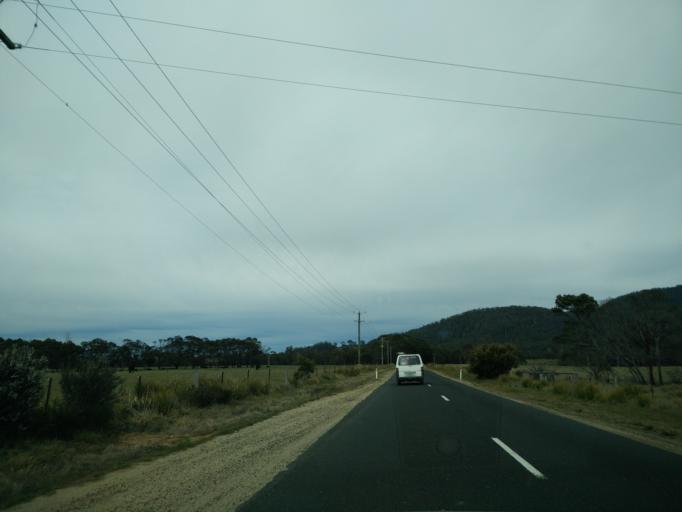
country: AU
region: Tasmania
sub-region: Break O'Day
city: St Helens
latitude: -41.8932
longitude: 148.2635
